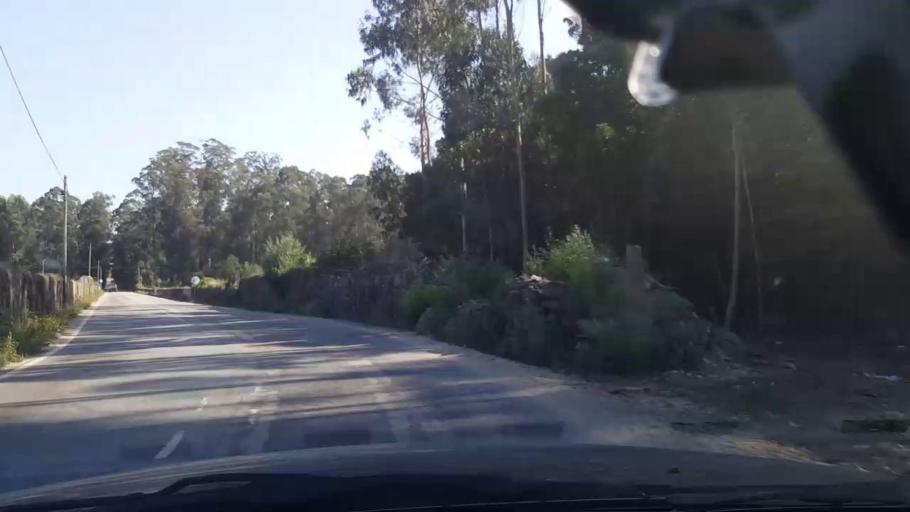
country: PT
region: Porto
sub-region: Vila do Conde
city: Arvore
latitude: 41.3598
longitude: -8.6766
